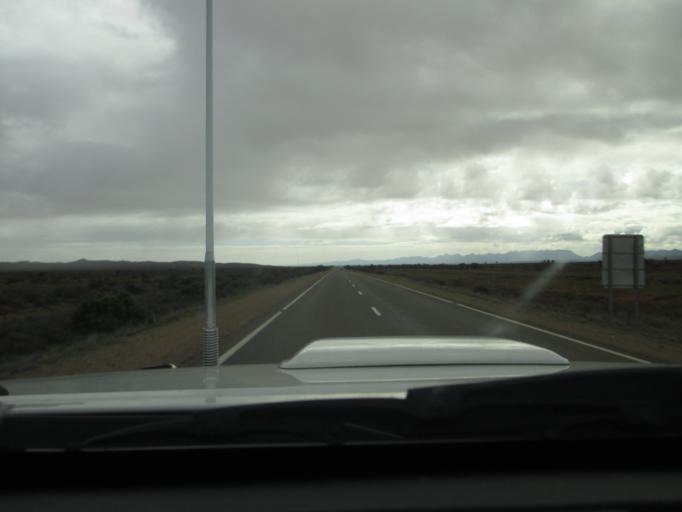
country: AU
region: South Australia
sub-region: Flinders Ranges
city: Quorn
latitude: -31.5396
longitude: 138.4249
